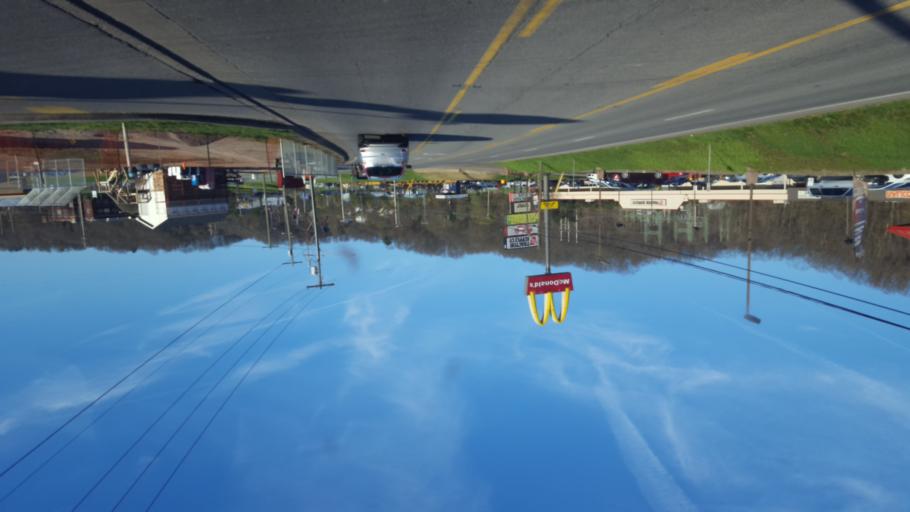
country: US
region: West Virginia
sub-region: Brooke County
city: Follansbee
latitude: 40.3385
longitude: -80.5972
